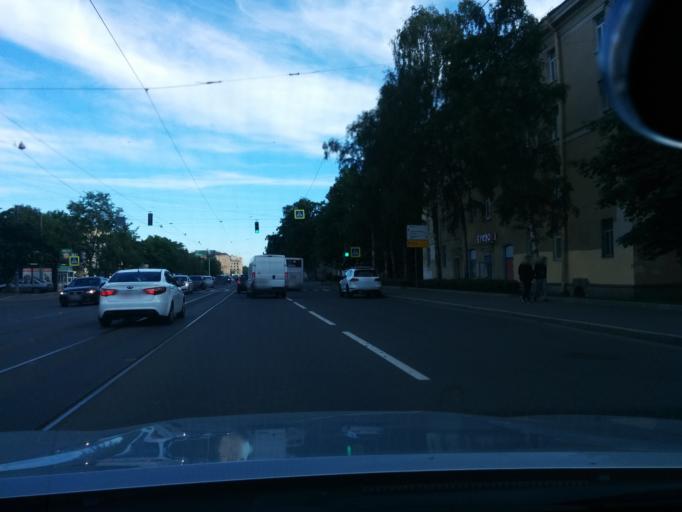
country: RU
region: Leningrad
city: Svetlanovskiy
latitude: 60.0094
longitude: 30.3253
